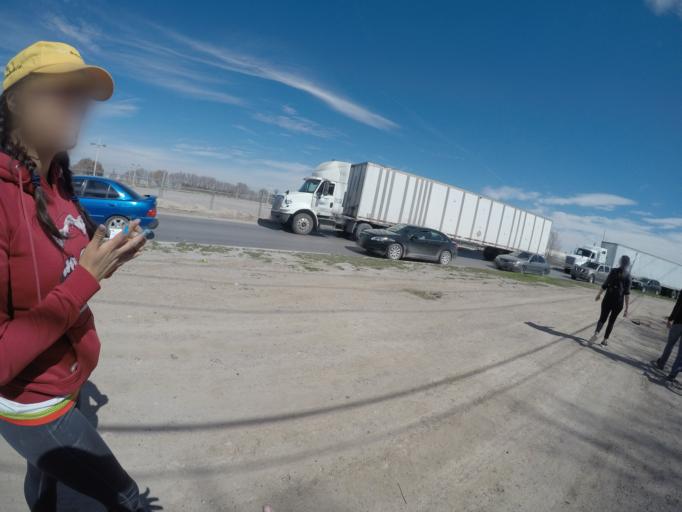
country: US
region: Texas
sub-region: El Paso County
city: Socorro
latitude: 31.6485
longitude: -106.3533
